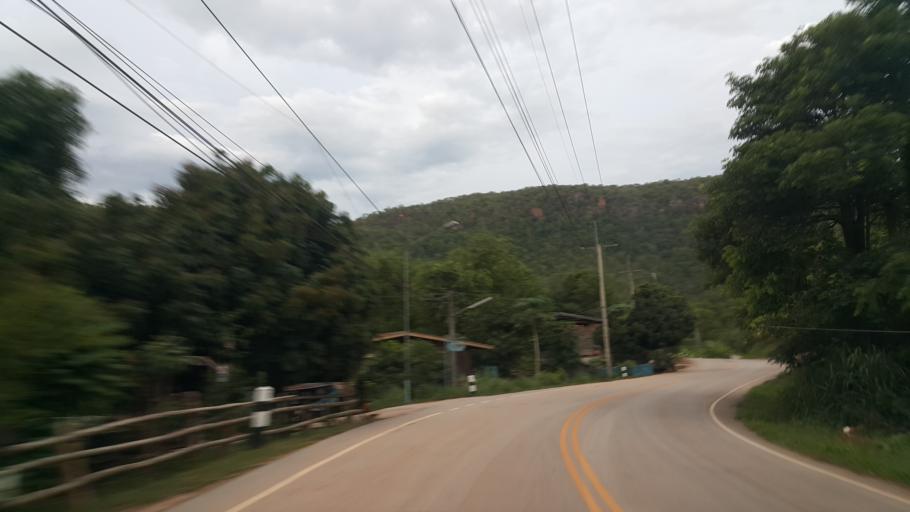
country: TH
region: Loei
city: Na Haeo
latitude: 17.4942
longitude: 101.1808
